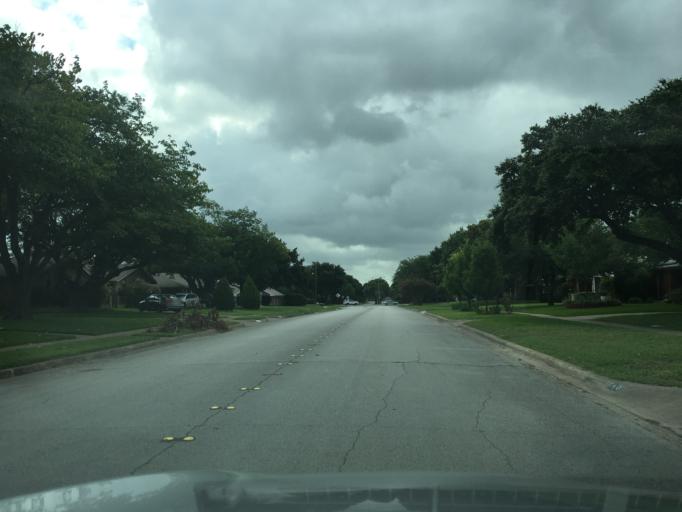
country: US
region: Texas
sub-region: Dallas County
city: Richardson
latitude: 32.9399
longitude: -96.7202
